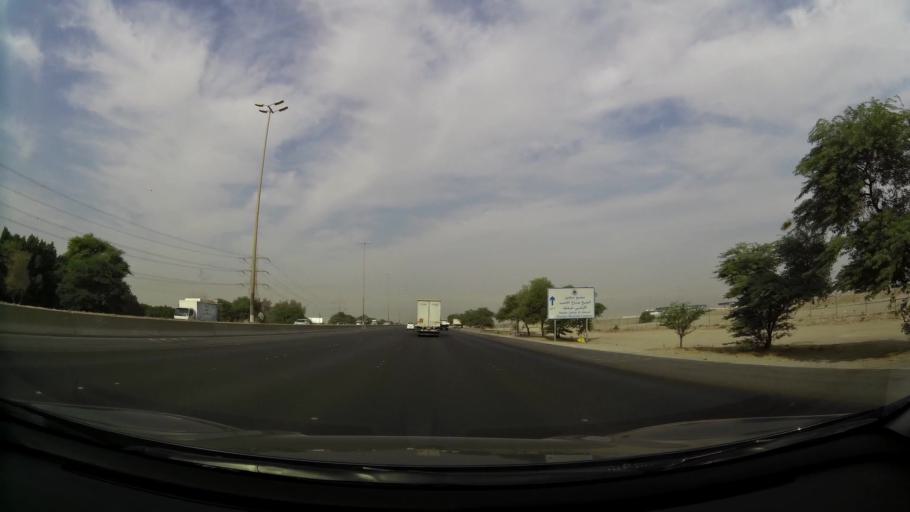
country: KW
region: Al Asimah
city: Ar Rabiyah
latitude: 29.2742
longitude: 47.8113
